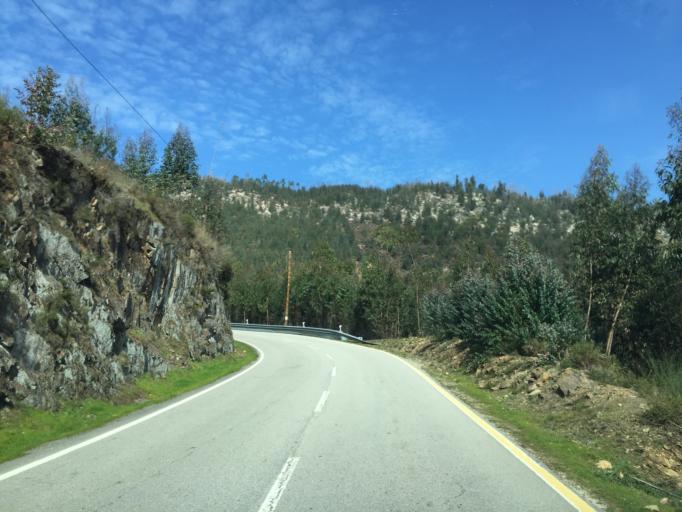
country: PT
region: Aveiro
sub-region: Arouca
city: Arouca
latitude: 40.9574
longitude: -8.1806
